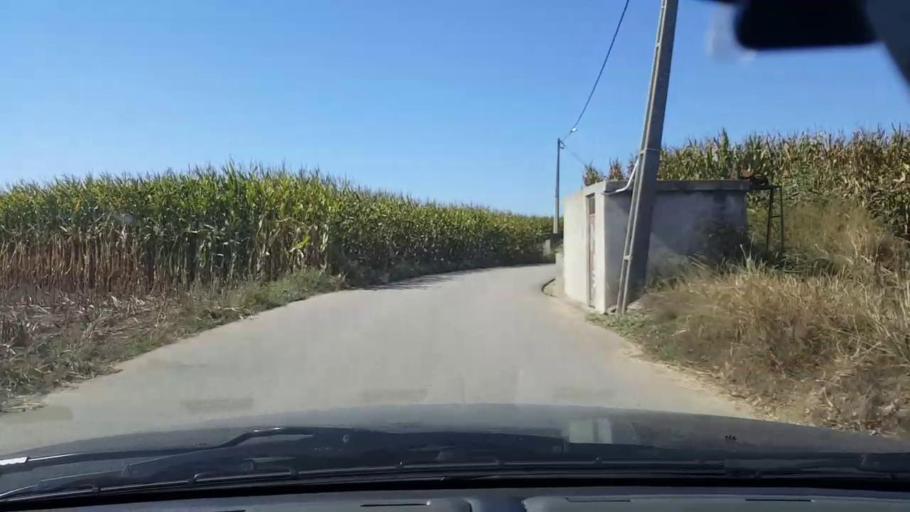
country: PT
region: Porto
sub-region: Matosinhos
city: Lavra
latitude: 41.2902
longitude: -8.6935
